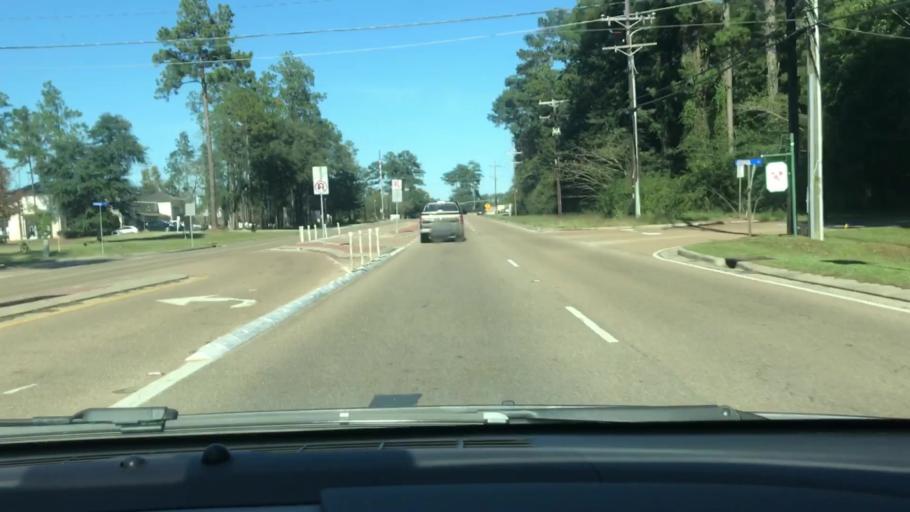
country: US
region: Louisiana
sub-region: Saint Tammany Parish
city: Covington
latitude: 30.4557
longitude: -90.1334
